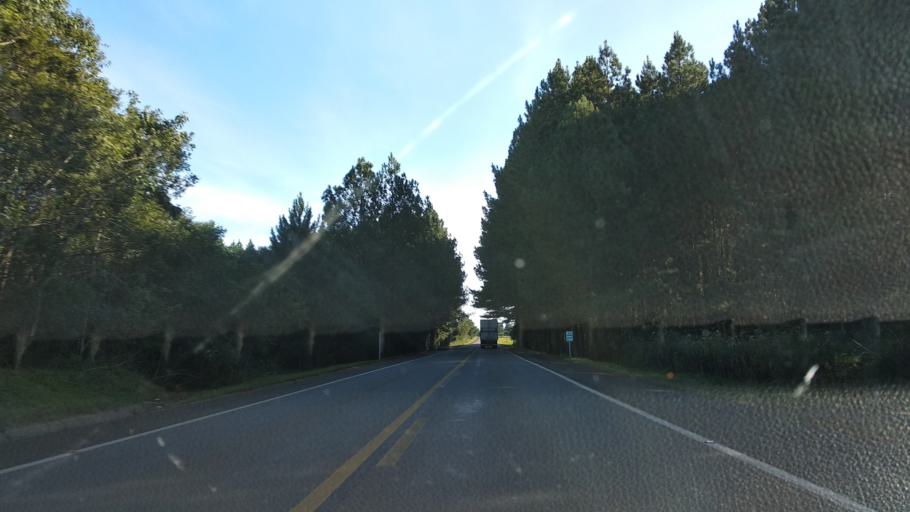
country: BR
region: Santa Catarina
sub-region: Celso Ramos
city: Celso Ramos
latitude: -27.5388
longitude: -51.4091
